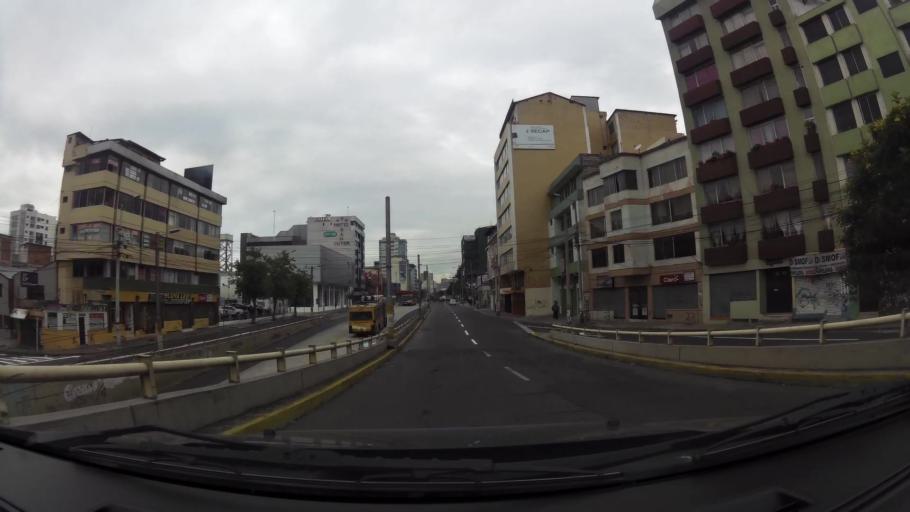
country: EC
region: Pichincha
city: Quito
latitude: -0.1964
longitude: -78.4953
